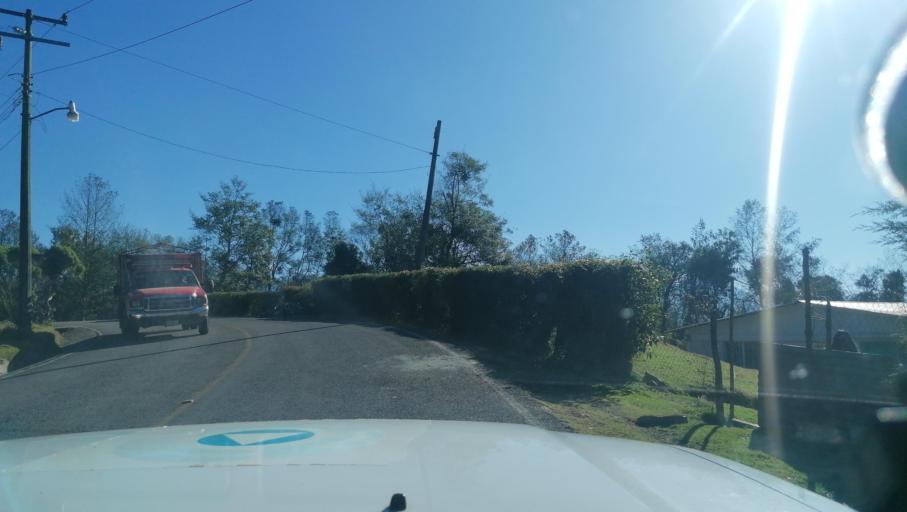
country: MX
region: Chiapas
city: Motozintla de Mendoza
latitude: 15.2480
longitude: -92.2261
